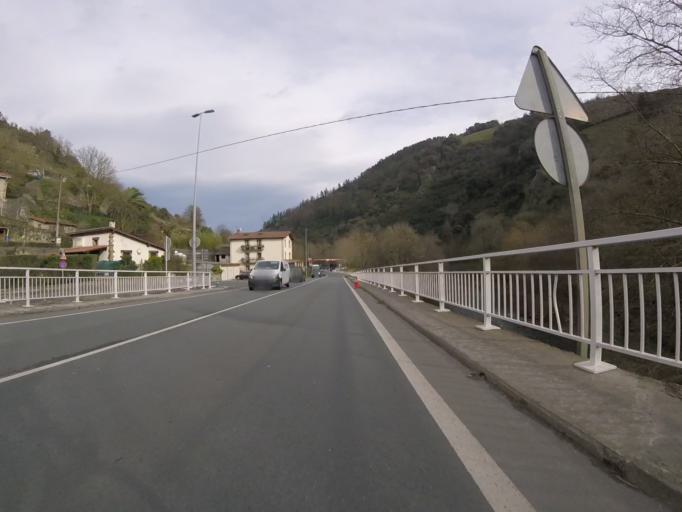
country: ES
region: Basque Country
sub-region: Provincia de Guipuzcoa
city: Azpeitia
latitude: 43.1884
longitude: -2.2601
